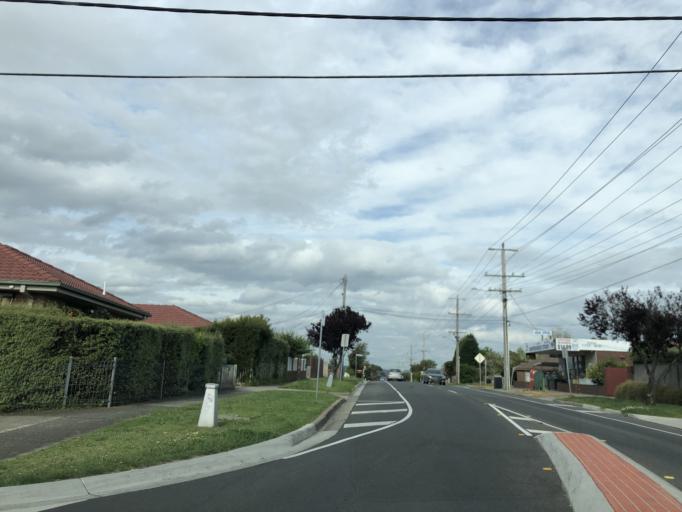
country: AU
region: Victoria
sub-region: Greater Dandenong
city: Noble Park North
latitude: -37.9551
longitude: 145.1962
